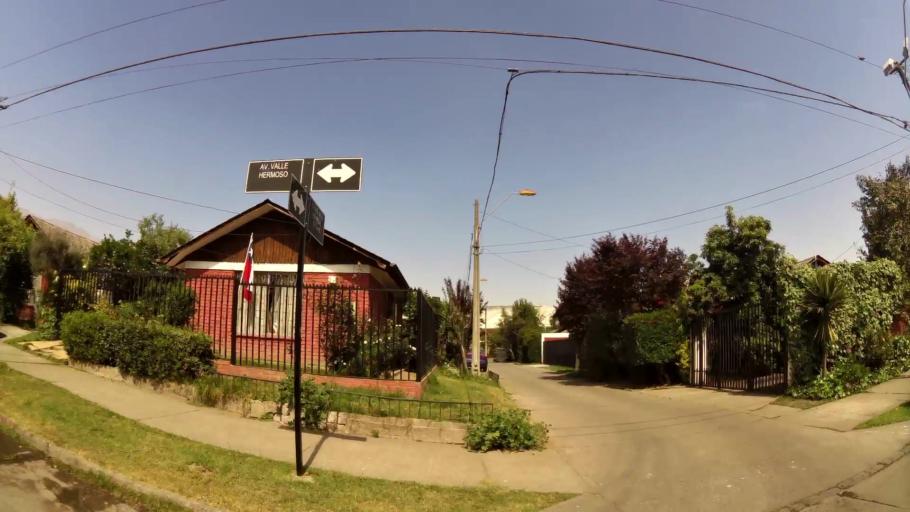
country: CL
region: Santiago Metropolitan
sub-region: Provincia de Santiago
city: Villa Presidente Frei, Nunoa, Santiago, Chile
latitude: -33.4644
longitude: -70.5448
